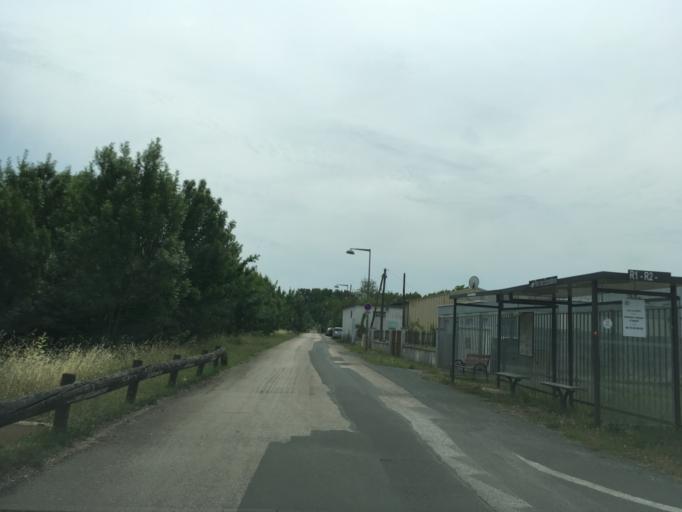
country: FR
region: Poitou-Charentes
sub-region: Departement des Deux-Sevres
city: Niort
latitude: 46.3298
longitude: -0.4893
